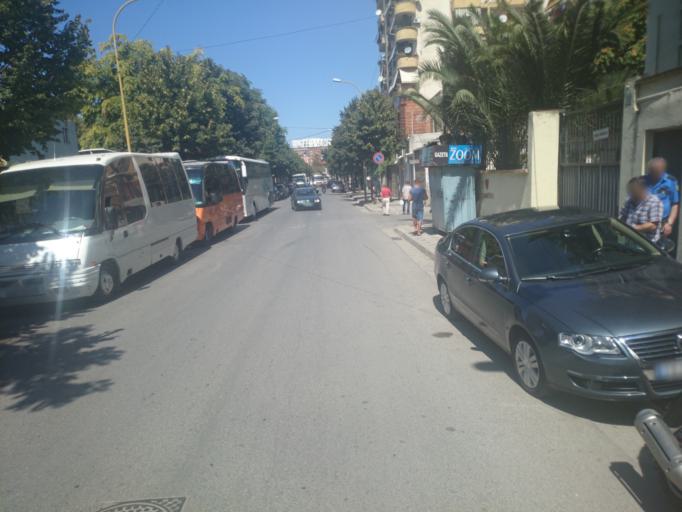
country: AL
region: Tirane
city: Tirana
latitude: 41.3221
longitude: 19.7984
